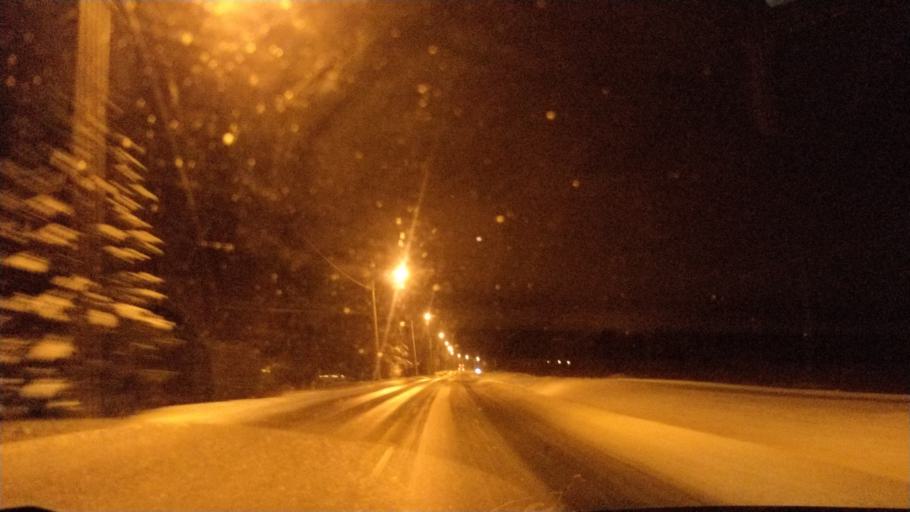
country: FI
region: Lapland
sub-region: Rovaniemi
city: Rovaniemi
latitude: 66.3152
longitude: 25.3619
